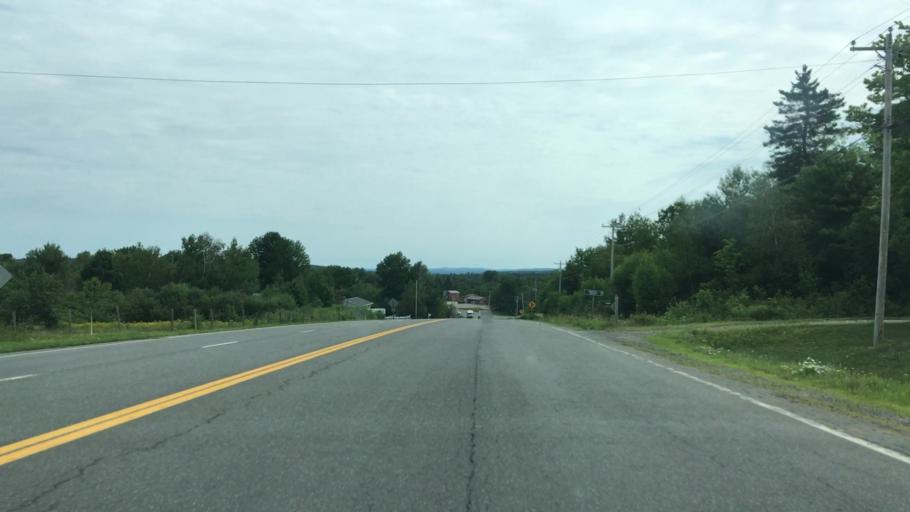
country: US
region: Maine
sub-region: Washington County
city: Calais
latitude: 45.0927
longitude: -67.4748
